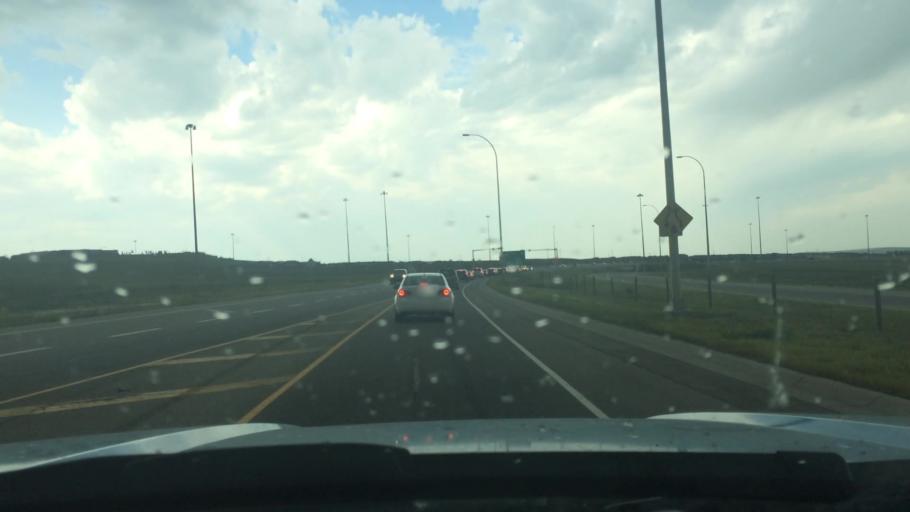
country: CA
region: Alberta
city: Calgary
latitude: 51.1477
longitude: -114.1366
